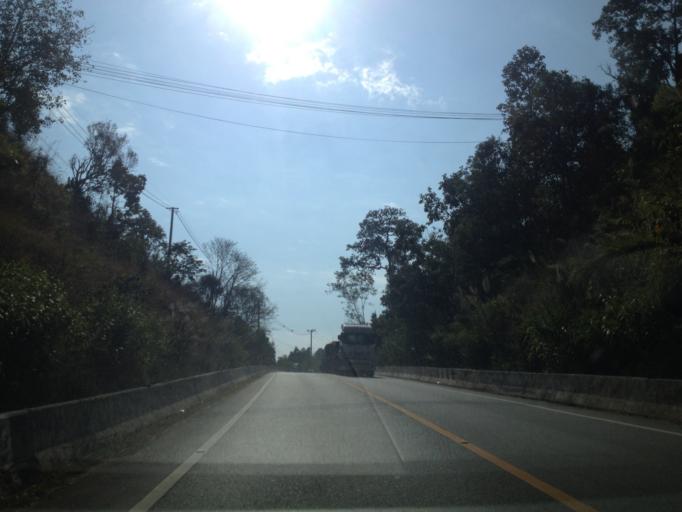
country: TH
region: Mae Hong Son
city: Pa Pae
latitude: 18.1656
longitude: 98.2318
